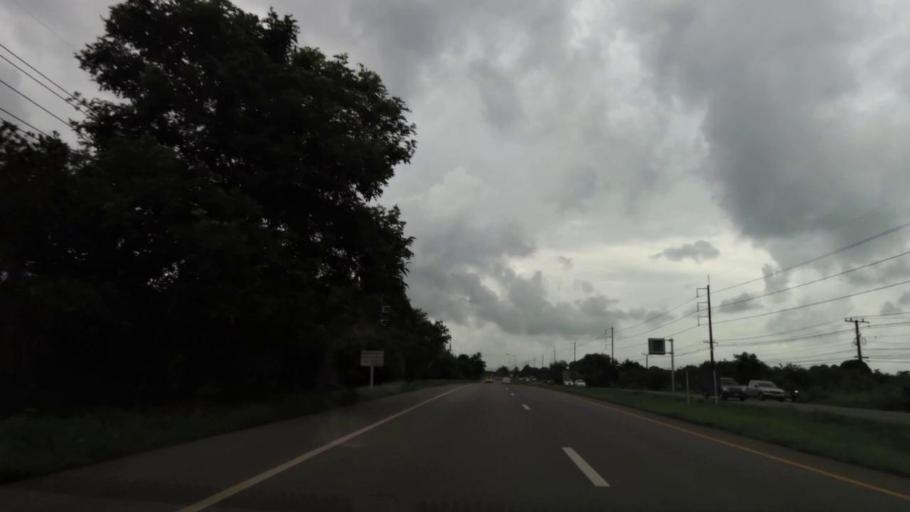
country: TH
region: Chanthaburi
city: Tha Mai
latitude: 12.6899
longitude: 101.9968
